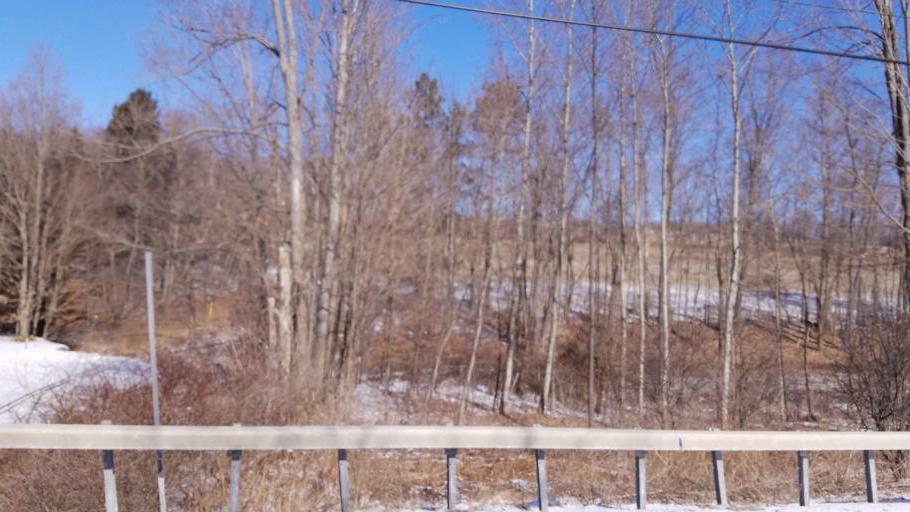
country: US
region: New York
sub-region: Allegany County
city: Andover
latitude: 42.0655
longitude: -77.8204
